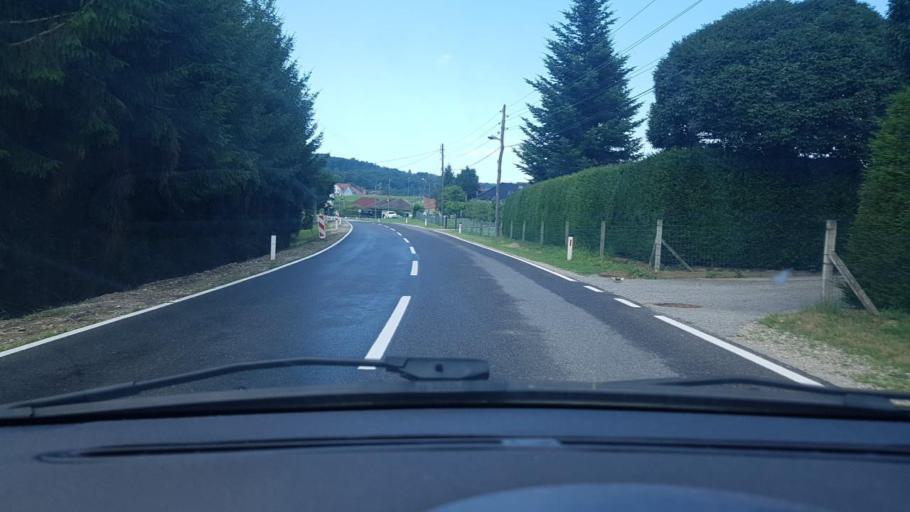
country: SI
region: Sentilj
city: Selnica ob Muri
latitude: 46.6900
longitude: 15.6966
